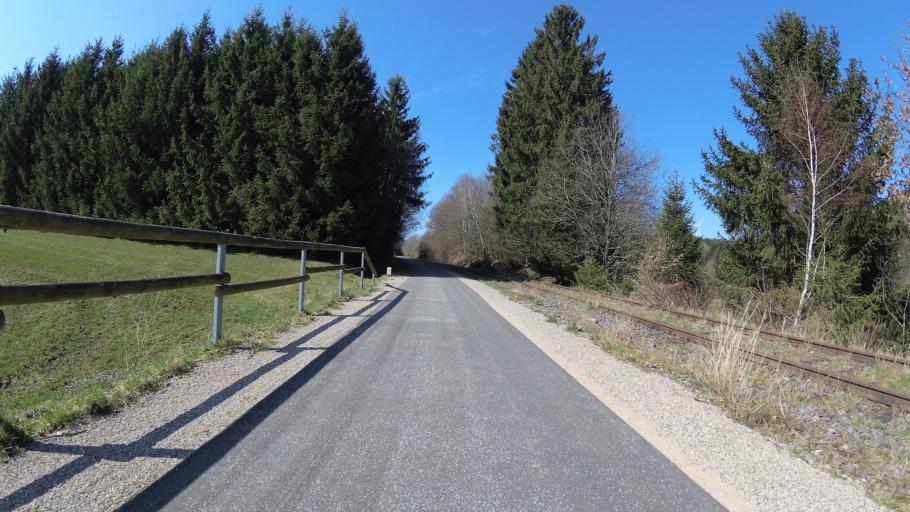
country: DE
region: Rheinland-Pfalz
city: Hermeskeil
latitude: 49.6674
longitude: 6.9285
